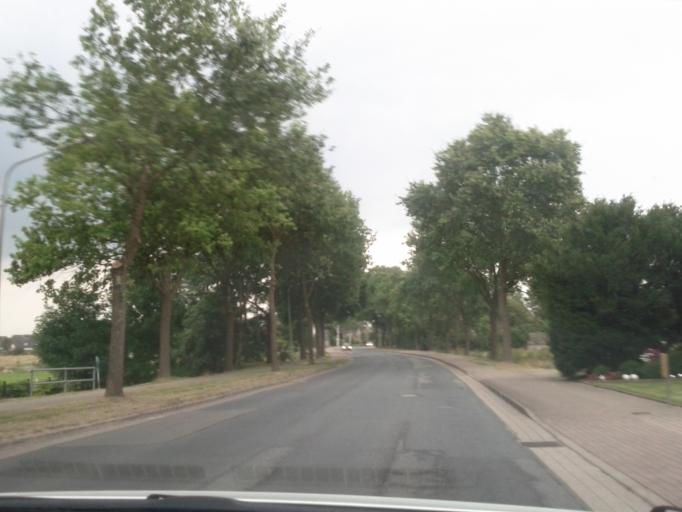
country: DE
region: Lower Saxony
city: Bargstedt
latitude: 53.4367
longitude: 9.4661
